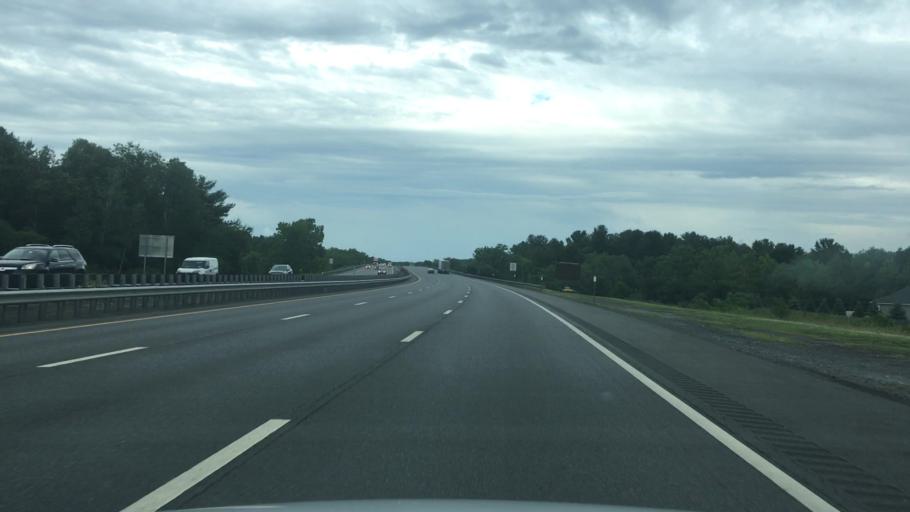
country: US
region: New York
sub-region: Schenectady County
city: Rotterdam
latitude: 42.7760
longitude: -73.9946
